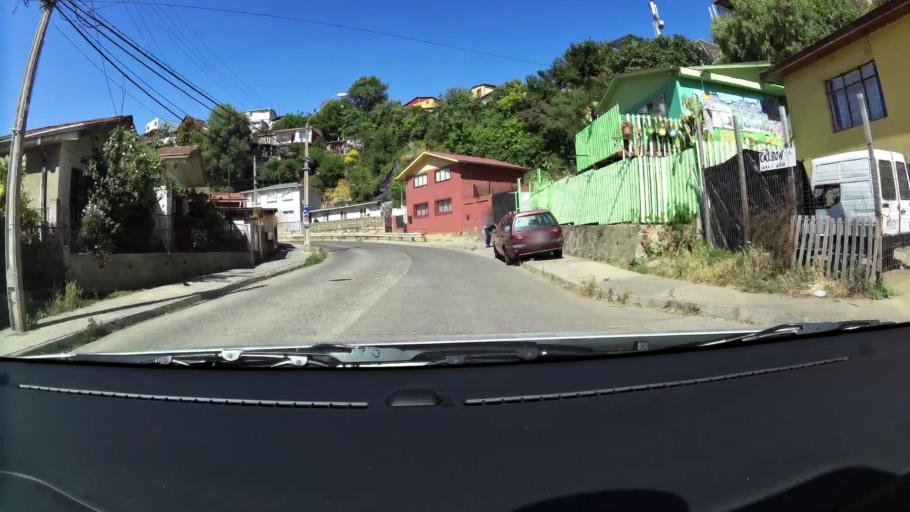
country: CL
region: Valparaiso
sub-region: Provincia de Valparaiso
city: Valparaiso
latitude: -33.0627
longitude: -71.5927
